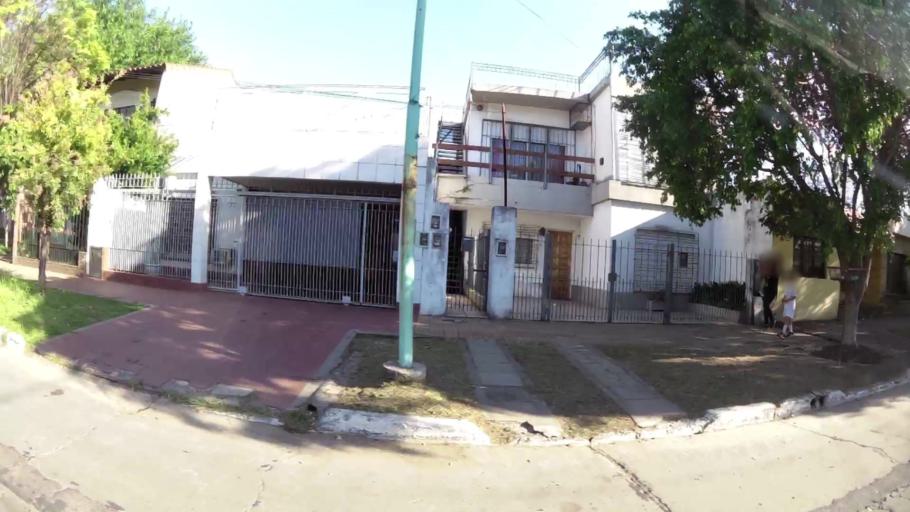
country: AR
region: Buenos Aires
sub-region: Partido de Merlo
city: Merlo
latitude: -34.6684
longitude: -58.7324
